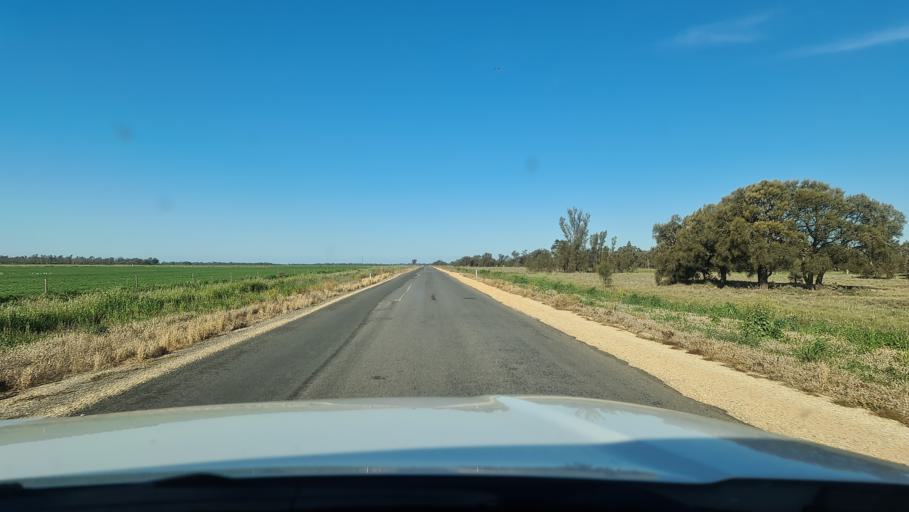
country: AU
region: Victoria
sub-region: Horsham
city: Horsham
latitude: -36.4492
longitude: 142.5468
